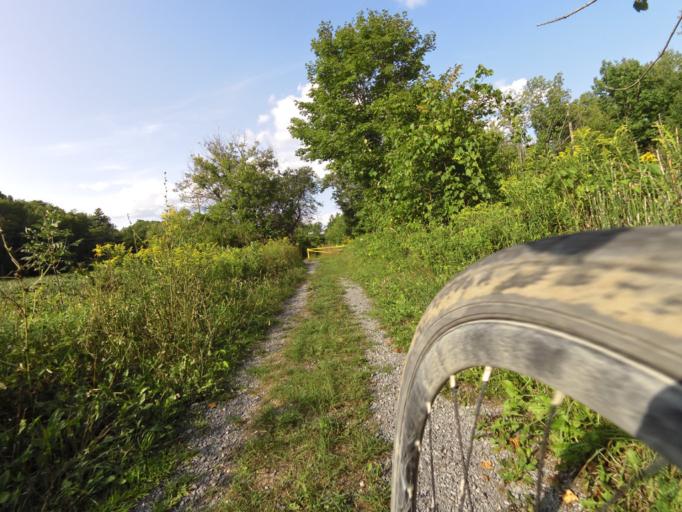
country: CA
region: Ontario
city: Kingston
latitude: 44.4520
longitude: -76.5229
